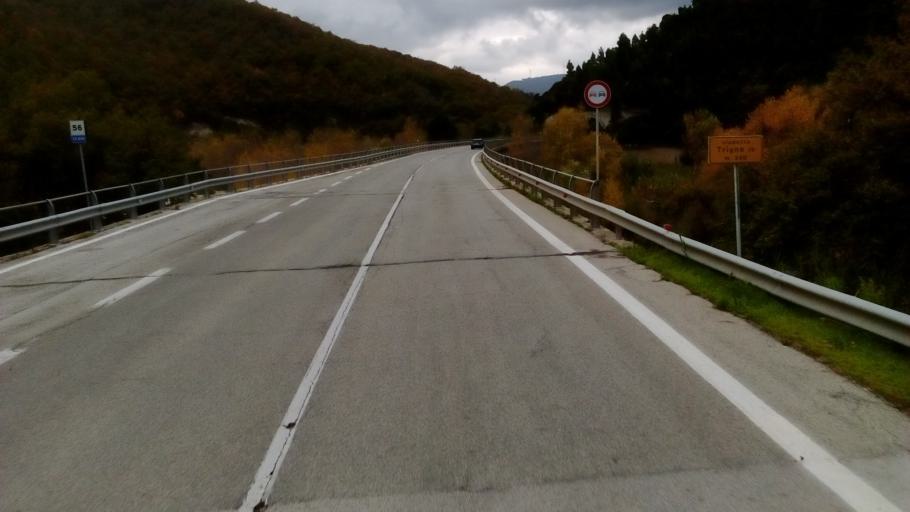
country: IT
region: Molise
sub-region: Provincia di Campobasso
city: Montemitro
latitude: 41.9015
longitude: 14.6427
